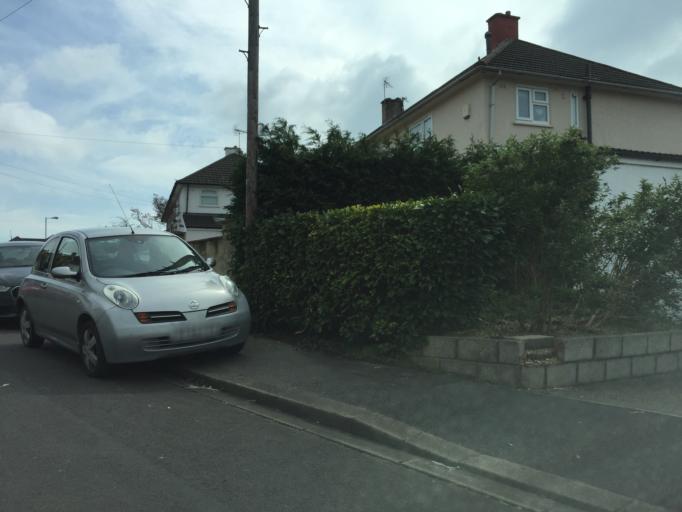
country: GB
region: England
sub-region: South Gloucestershire
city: Almondsbury
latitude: 51.5141
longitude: -2.5992
